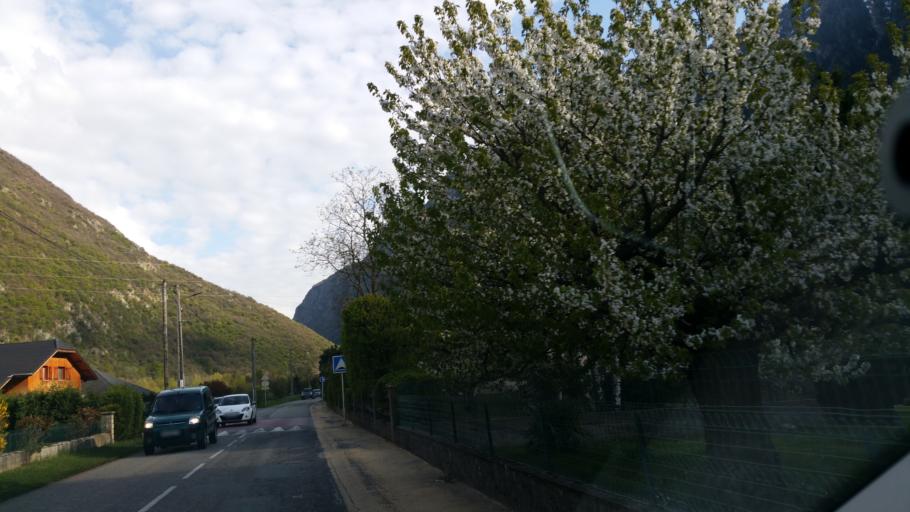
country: FR
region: Rhone-Alpes
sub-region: Departement de la Savoie
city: La Chambre
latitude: 45.3299
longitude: 6.3134
